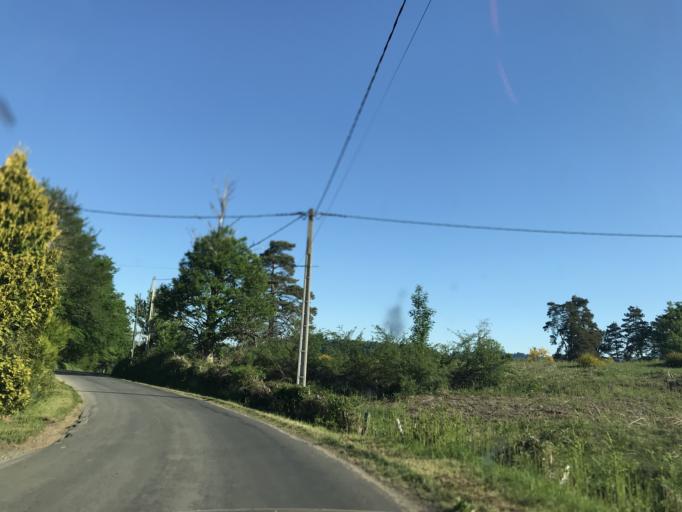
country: FR
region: Auvergne
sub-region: Departement du Puy-de-Dome
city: Job
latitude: 45.6563
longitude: 3.6645
